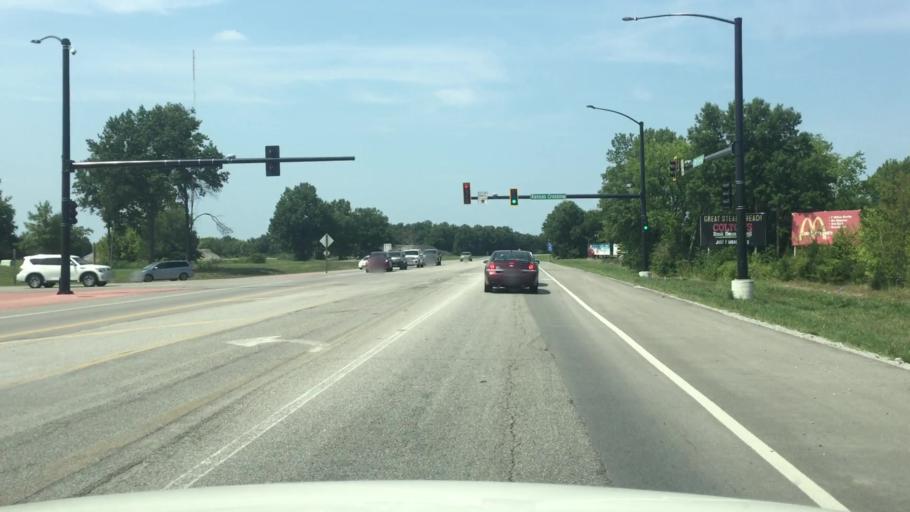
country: US
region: Kansas
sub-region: Crawford County
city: Pittsburg
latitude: 37.3450
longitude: -94.7069
